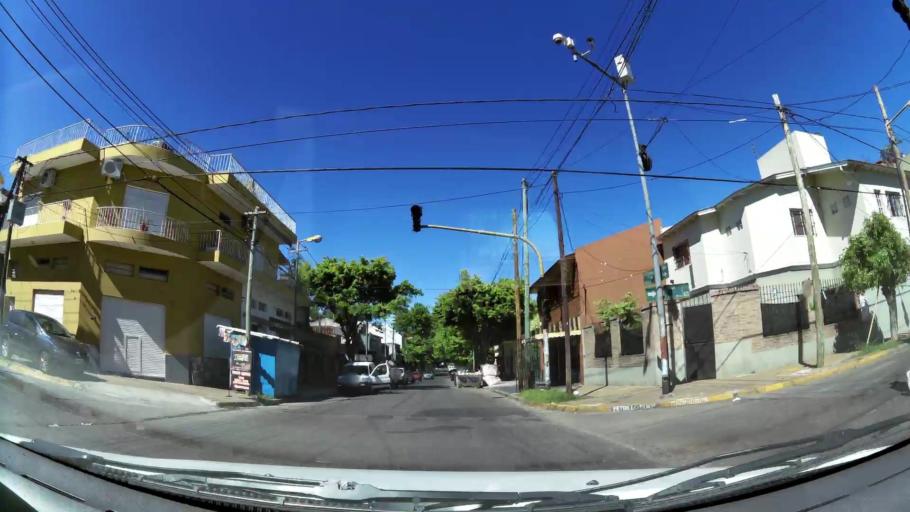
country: AR
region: Buenos Aires
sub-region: Partido de General San Martin
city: General San Martin
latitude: -34.5669
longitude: -58.5338
